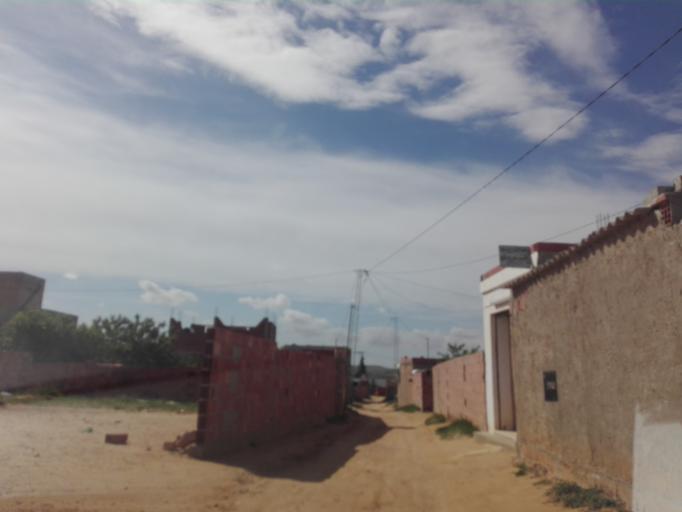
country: TN
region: Safaqis
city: Sfax
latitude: 34.7423
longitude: 10.5080
